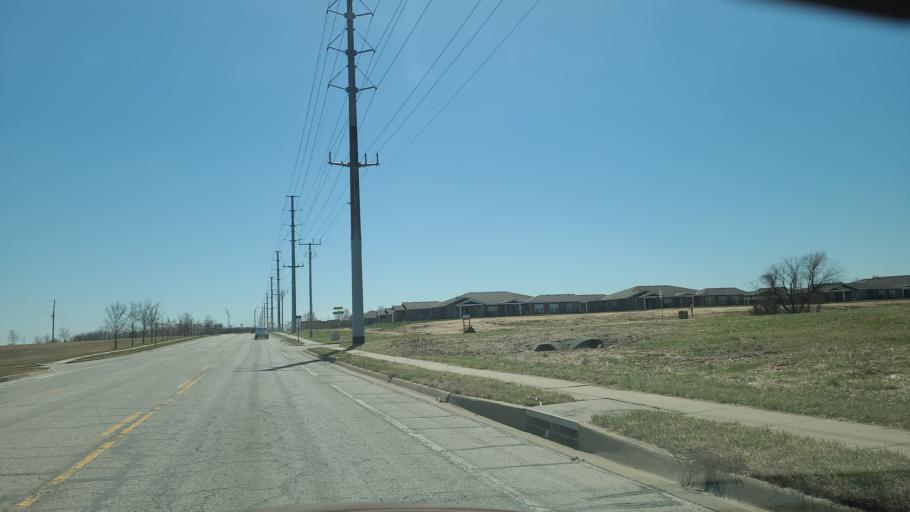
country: US
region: Kansas
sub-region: Douglas County
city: Lawrence
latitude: 38.9417
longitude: -95.2050
